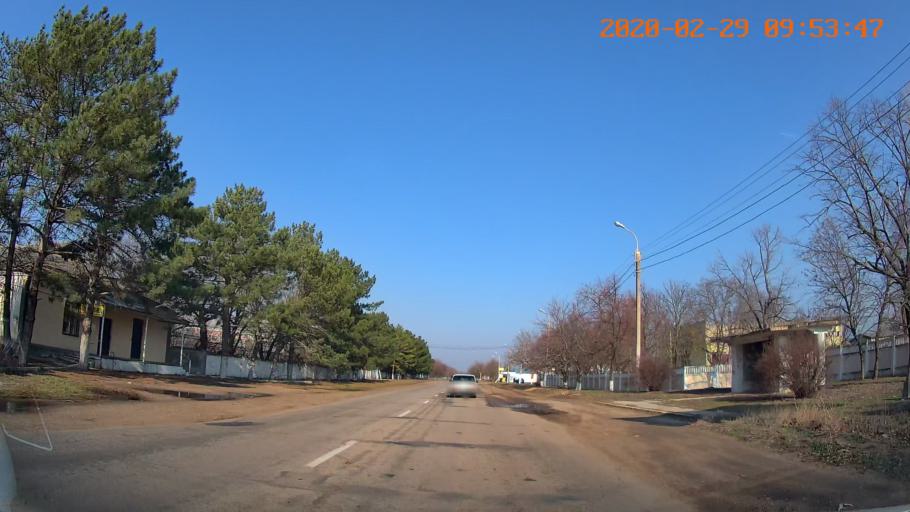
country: MD
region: Telenesti
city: Slobozia
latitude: 46.7242
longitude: 29.7198
